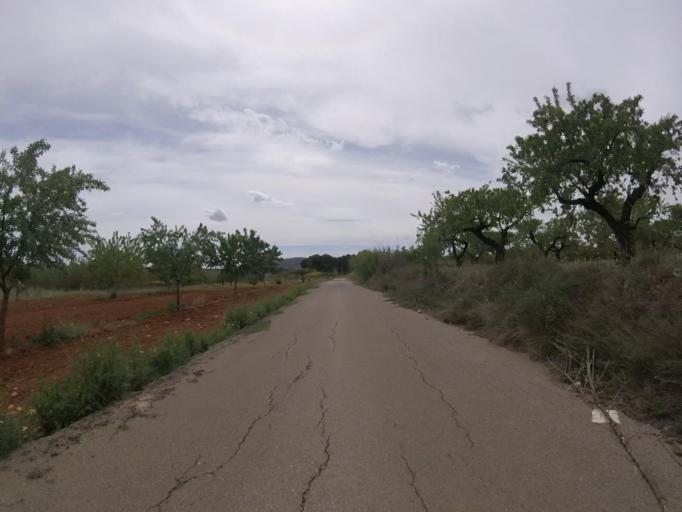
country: ES
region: Valencia
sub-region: Provincia de Castello
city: Benlloch
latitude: 40.1796
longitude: -0.0066
